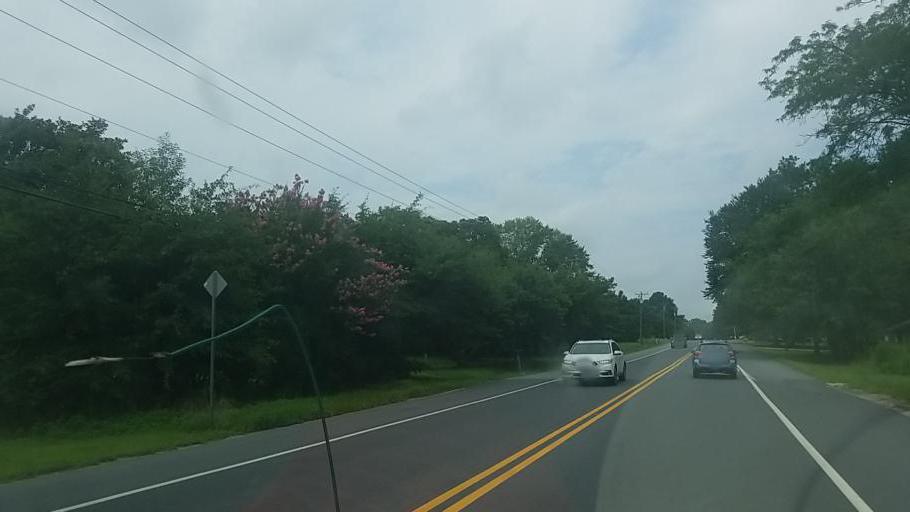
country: US
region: Delaware
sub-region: Sussex County
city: Ocean View
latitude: 38.5503
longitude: -75.1491
